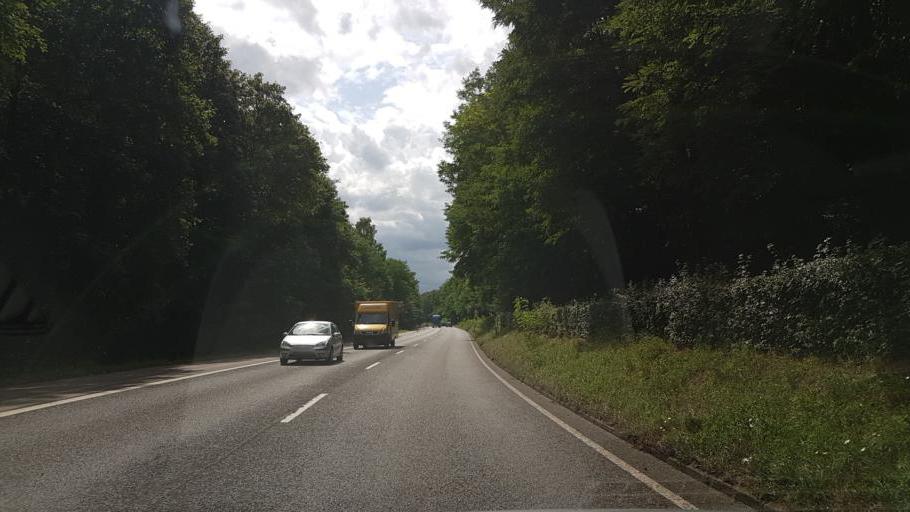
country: DE
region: Saarland
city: Saarwellingen
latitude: 49.3338
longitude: 6.7812
